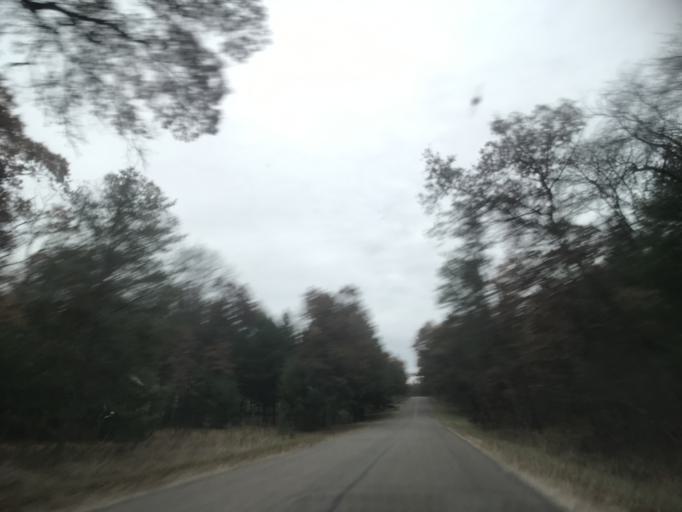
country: US
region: Wisconsin
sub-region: Oconto County
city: Gillett
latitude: 45.2668
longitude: -88.2543
